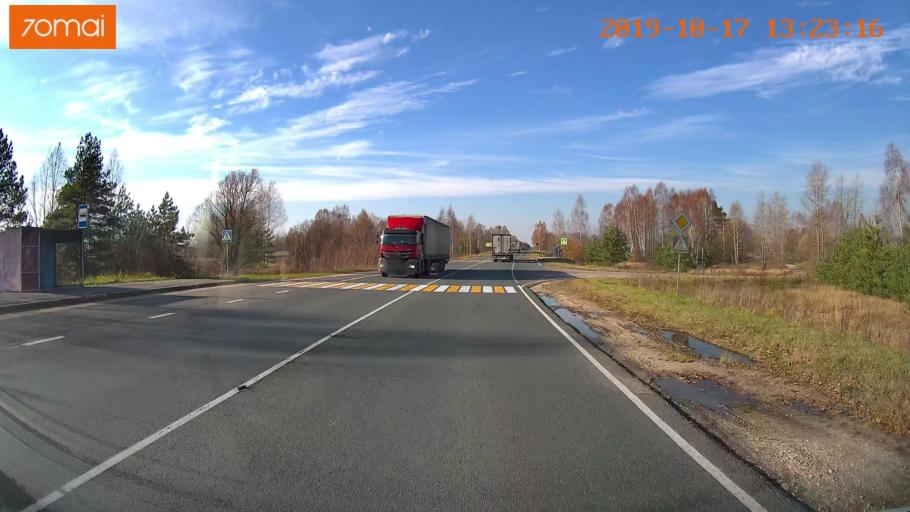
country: RU
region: Rjazan
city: Gus'-Zheleznyy
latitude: 55.0885
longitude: 40.9823
